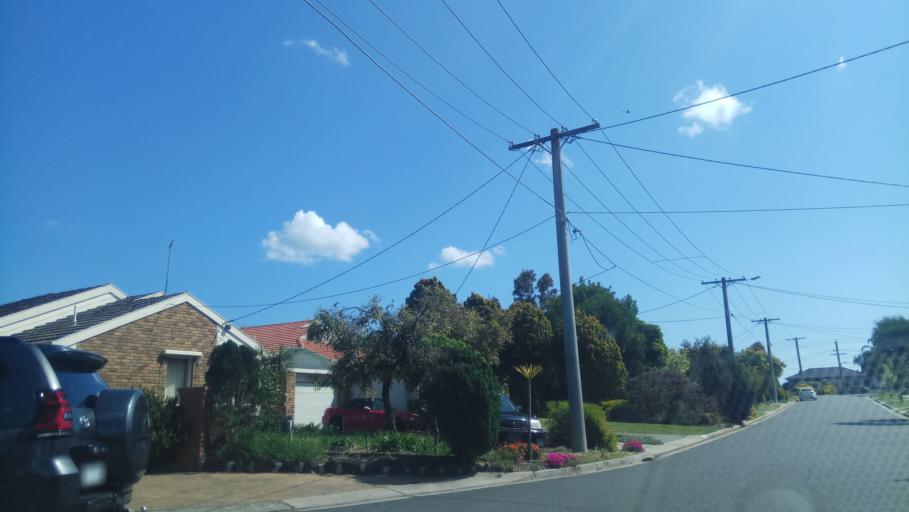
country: AU
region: Victoria
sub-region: Kingston
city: Dingley Village
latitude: -37.9760
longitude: 145.1189
